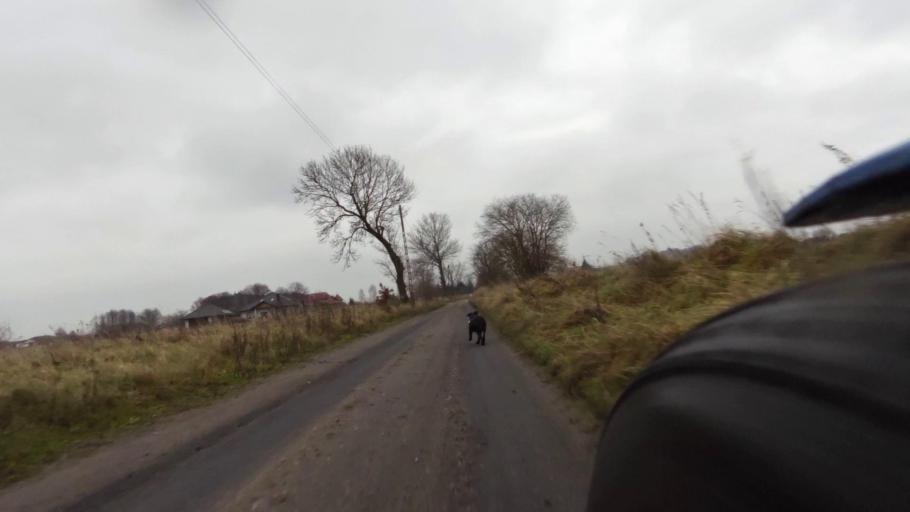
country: PL
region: West Pomeranian Voivodeship
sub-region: Powiat szczecinecki
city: Szczecinek
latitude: 53.6631
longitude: 16.6670
